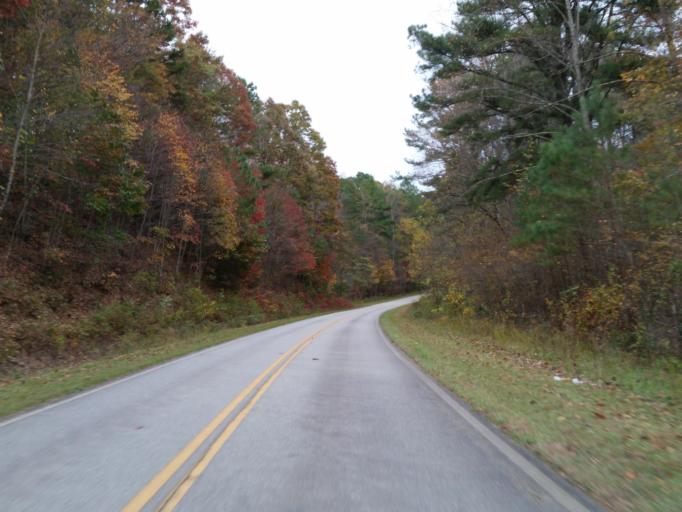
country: US
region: Georgia
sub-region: Fannin County
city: Blue Ridge
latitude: 34.6871
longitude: -84.2659
